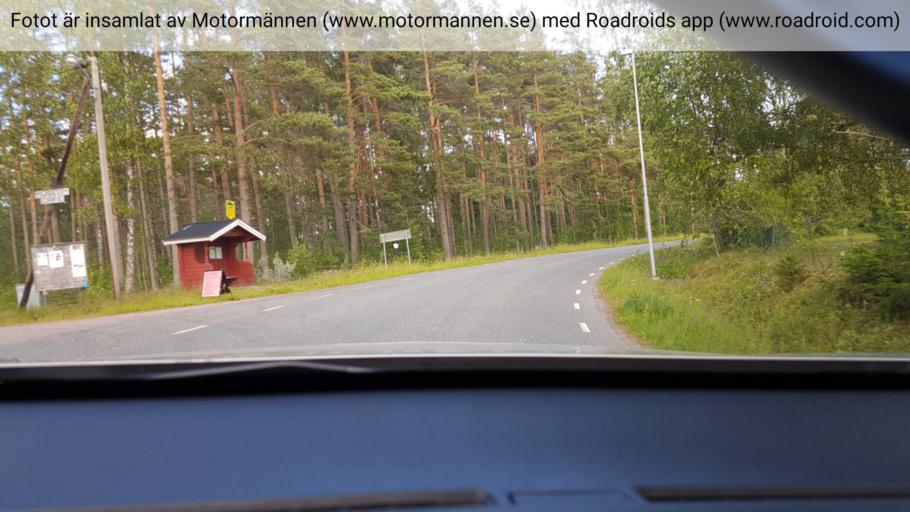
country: SE
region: Vaermland
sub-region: Filipstads Kommun
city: Filipstad
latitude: 59.8354
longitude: 14.1040
